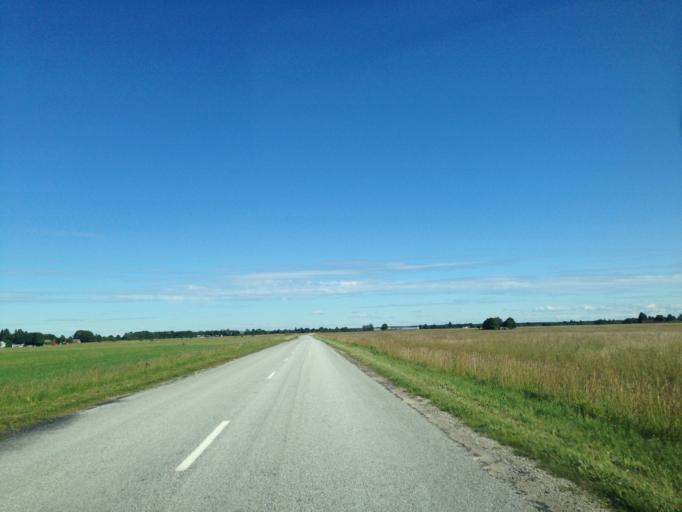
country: EE
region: Harju
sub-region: Kuusalu vald
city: Kuusalu
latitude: 59.4652
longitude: 25.3241
